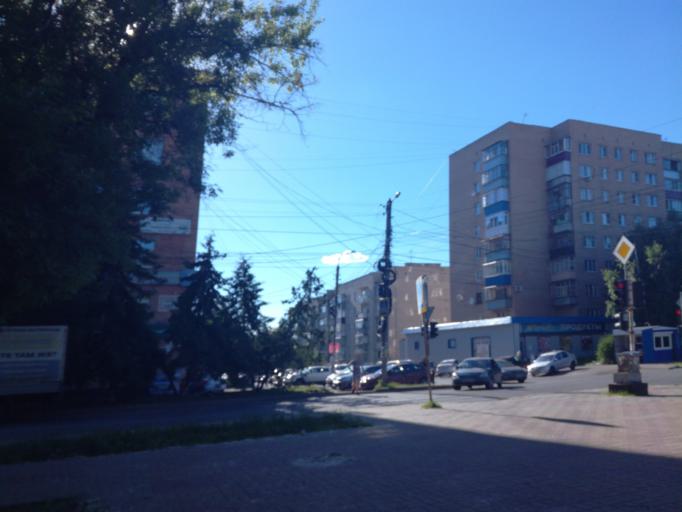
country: RU
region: Kursk
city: Kursk
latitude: 51.7462
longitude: 36.1874
